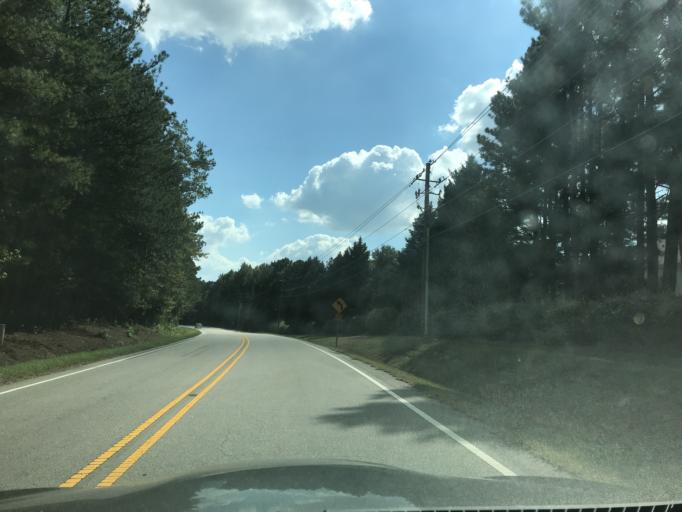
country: US
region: North Carolina
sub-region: Wake County
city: Wake Forest
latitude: 35.9135
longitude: -78.5294
